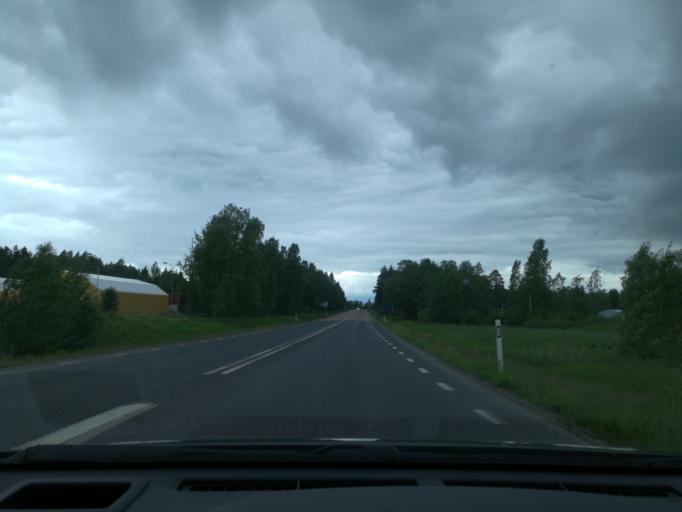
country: SE
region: Dalarna
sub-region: Smedjebackens Kommun
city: Smedjebacken
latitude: 60.1327
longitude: 15.3996
